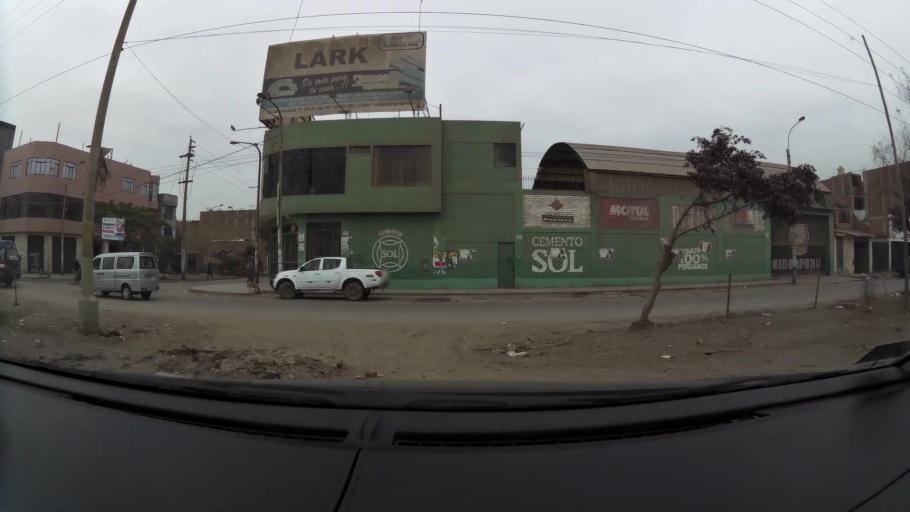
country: PE
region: Lima
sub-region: Lima
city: Independencia
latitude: -11.9493
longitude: -77.0859
